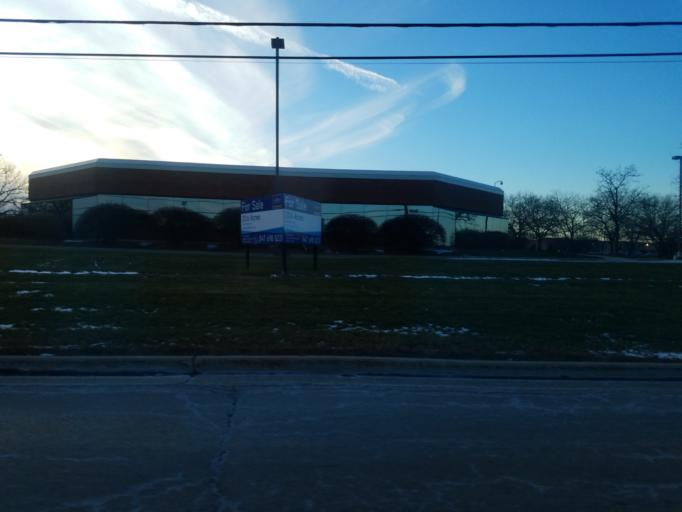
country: US
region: Illinois
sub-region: DuPage County
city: Wood Dale
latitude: 41.9768
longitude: -87.9797
